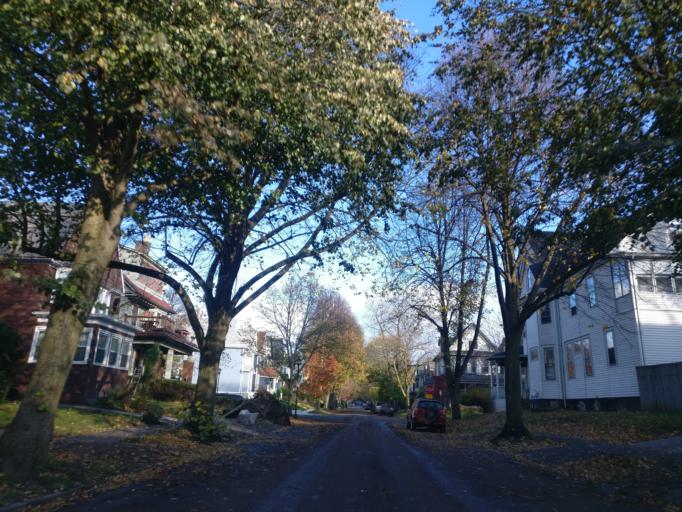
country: US
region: New York
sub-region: Erie County
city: Buffalo
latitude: 42.9123
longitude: -78.8811
